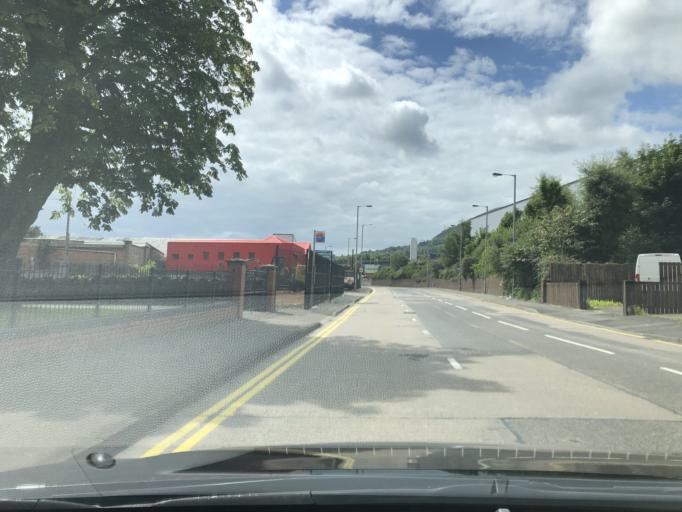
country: GB
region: Northern Ireland
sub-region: Newtownabbey District
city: Newtownabbey
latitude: 54.6528
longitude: -5.9155
